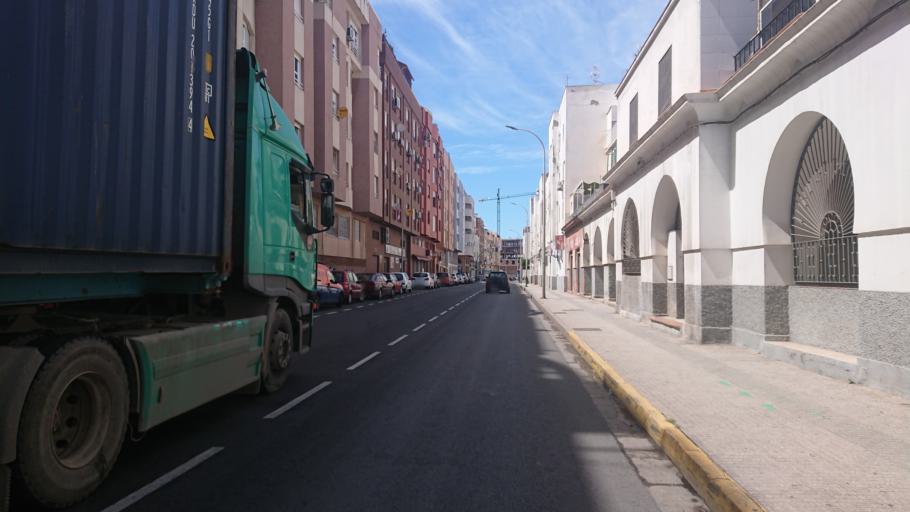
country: ES
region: Melilla
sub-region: Melilla
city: Melilla
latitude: 35.2800
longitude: -2.9394
